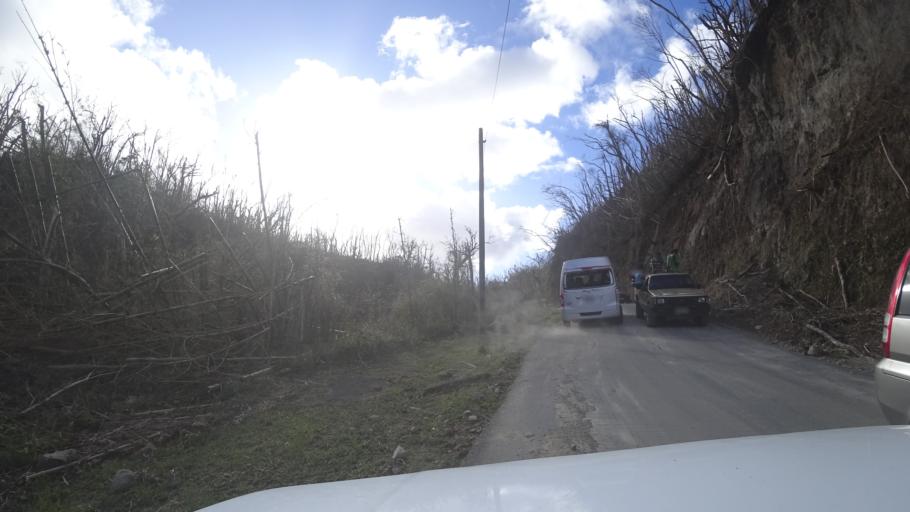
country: DM
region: Saint Luke
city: Pointe Michel
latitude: 15.2656
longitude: -61.3384
